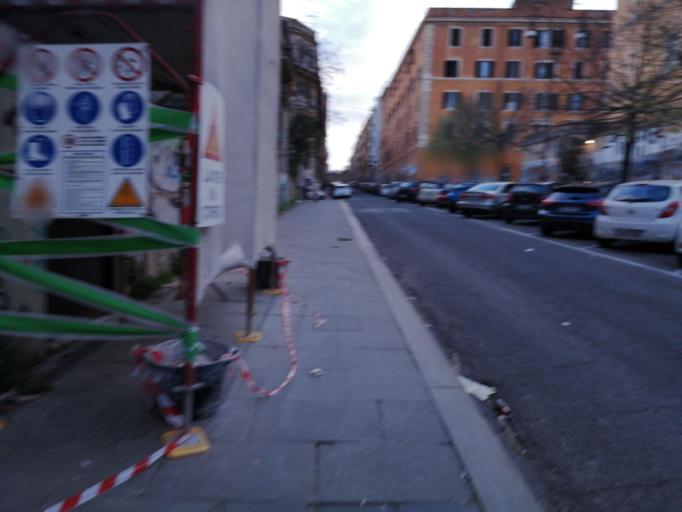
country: IT
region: Latium
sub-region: Citta metropolitana di Roma Capitale
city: Rome
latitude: 41.8967
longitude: 12.5162
